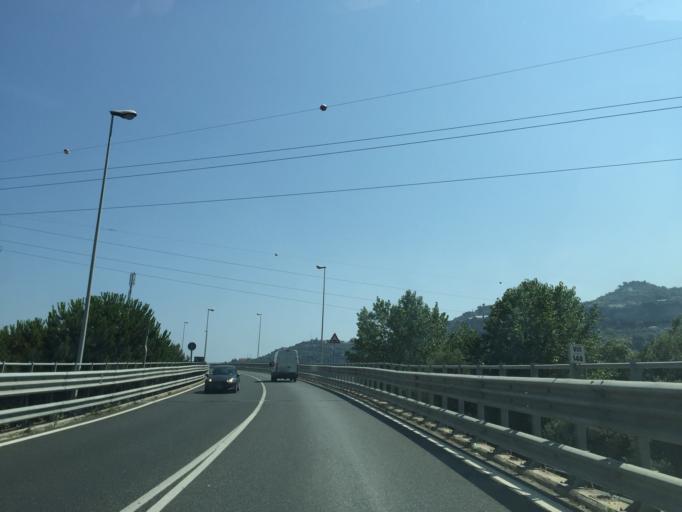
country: IT
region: Liguria
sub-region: Provincia di Imperia
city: Ventimiglia
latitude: 43.8086
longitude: 7.5922
